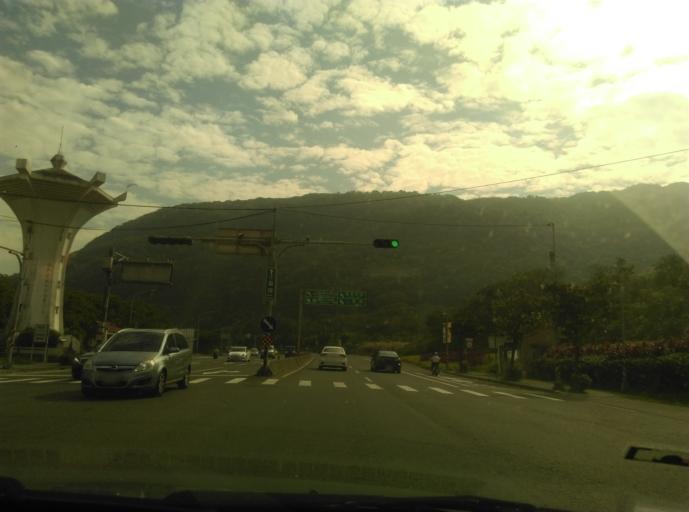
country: TW
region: Taiwan
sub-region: Keelung
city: Keelung
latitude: 25.1876
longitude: 121.6833
